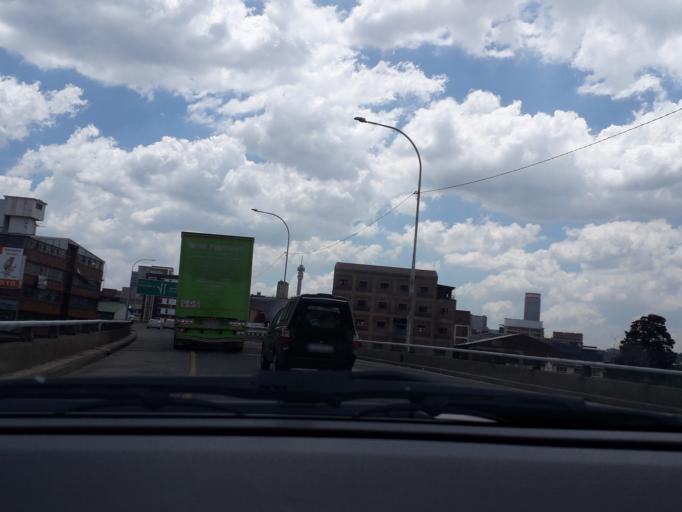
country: ZA
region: Gauteng
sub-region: City of Johannesburg Metropolitan Municipality
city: Johannesburg
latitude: -26.2098
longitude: 28.0557
